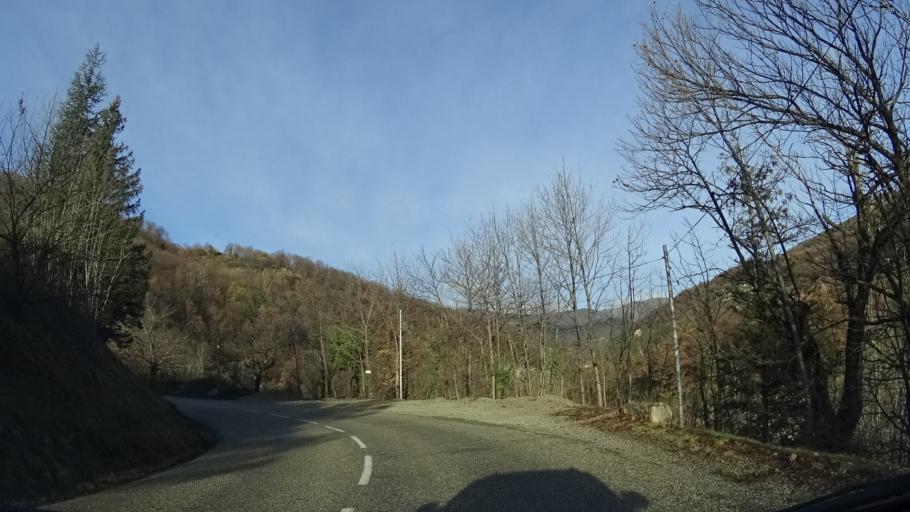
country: FR
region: Rhone-Alpes
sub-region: Departement de l'Ardeche
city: Thueyts
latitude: 44.7216
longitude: 4.2651
